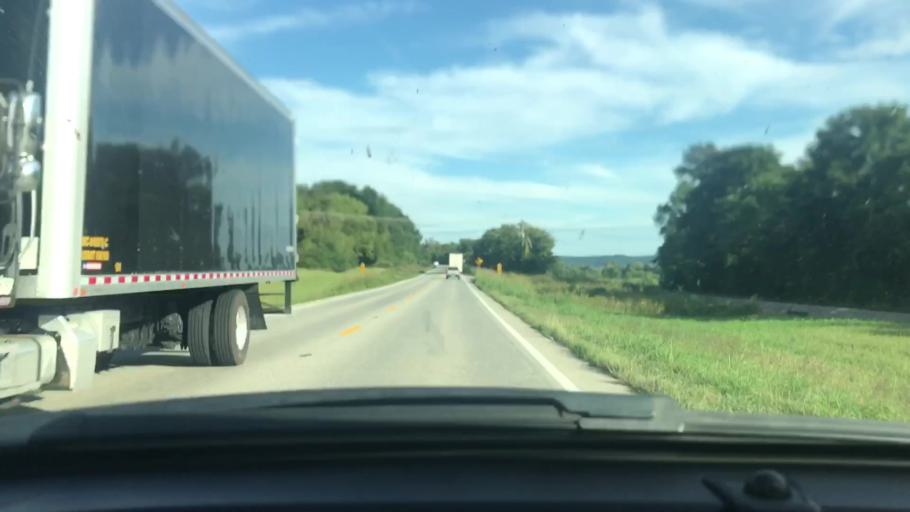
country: US
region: Arkansas
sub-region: Sharp County
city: Cherokee Village
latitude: 36.2995
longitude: -91.4403
